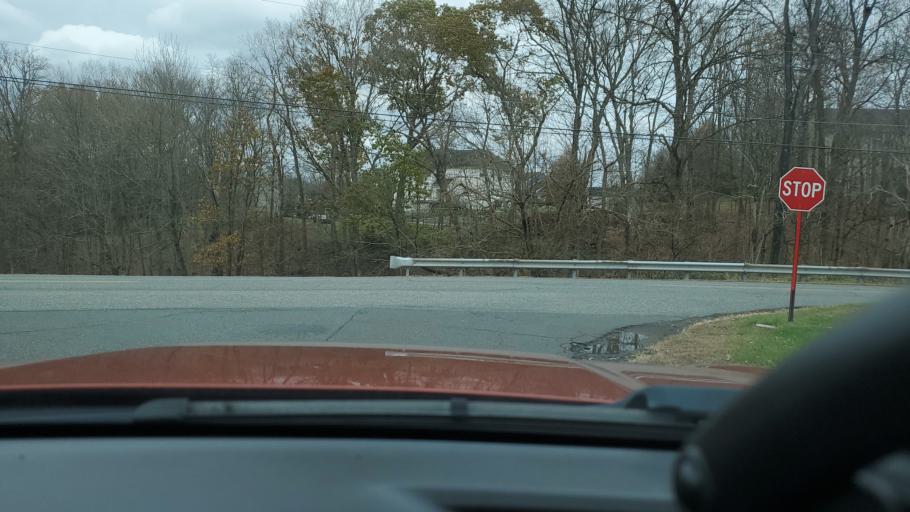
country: US
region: Pennsylvania
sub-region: Montgomery County
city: Spring Mount
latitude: 40.2922
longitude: -75.5076
